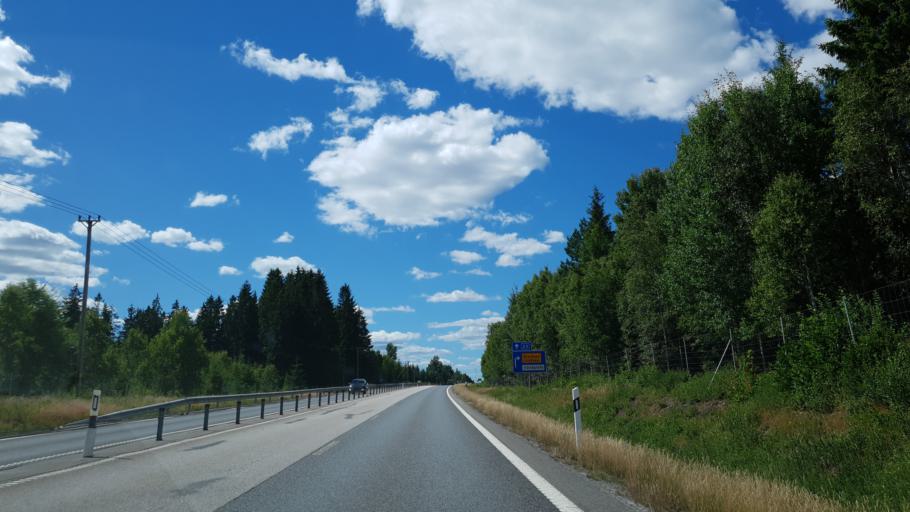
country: SE
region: Kronoberg
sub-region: Vaxjo Kommun
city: Vaexjoe
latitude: 56.8781
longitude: 14.9040
